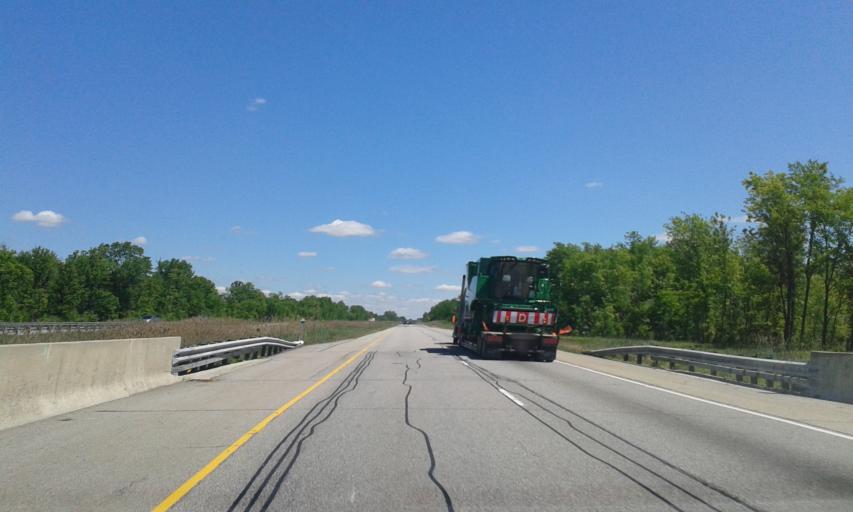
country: US
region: New York
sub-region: St. Lawrence County
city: Norfolk
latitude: 44.9300
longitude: -75.1667
